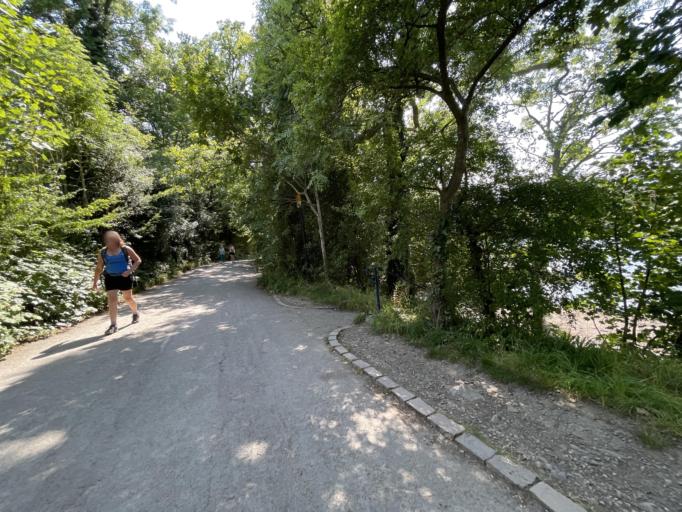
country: GB
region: England
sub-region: Cumbria
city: Keswick
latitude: 54.5931
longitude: -3.1403
